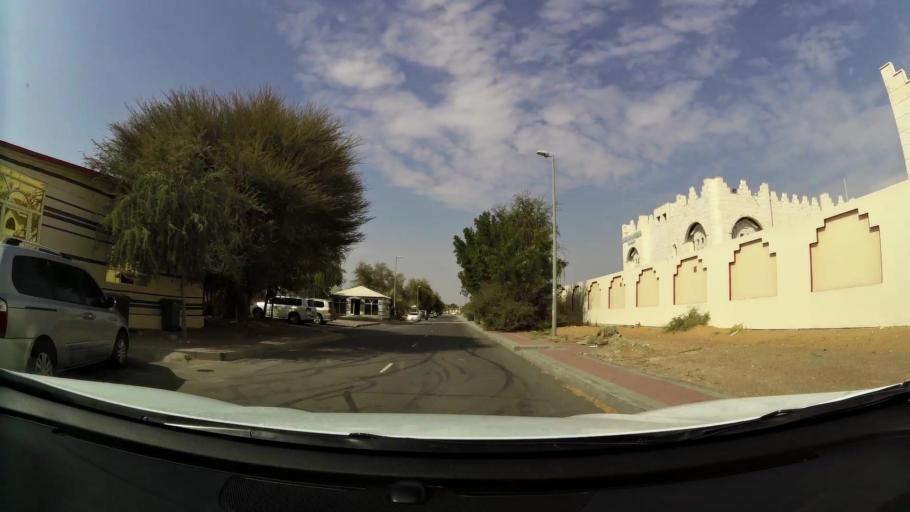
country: AE
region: Abu Dhabi
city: Al Ain
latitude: 24.0962
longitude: 55.9102
